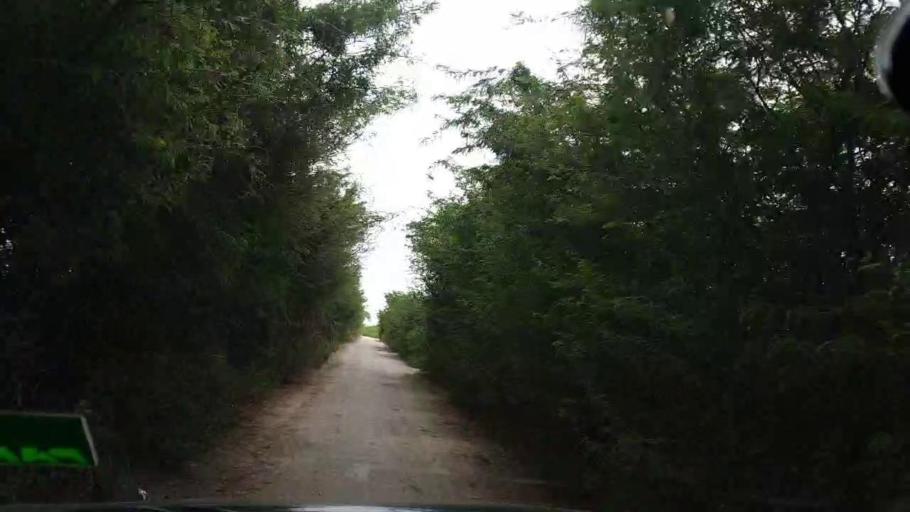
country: PK
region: Sindh
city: Kadhan
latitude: 24.5424
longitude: 69.2068
